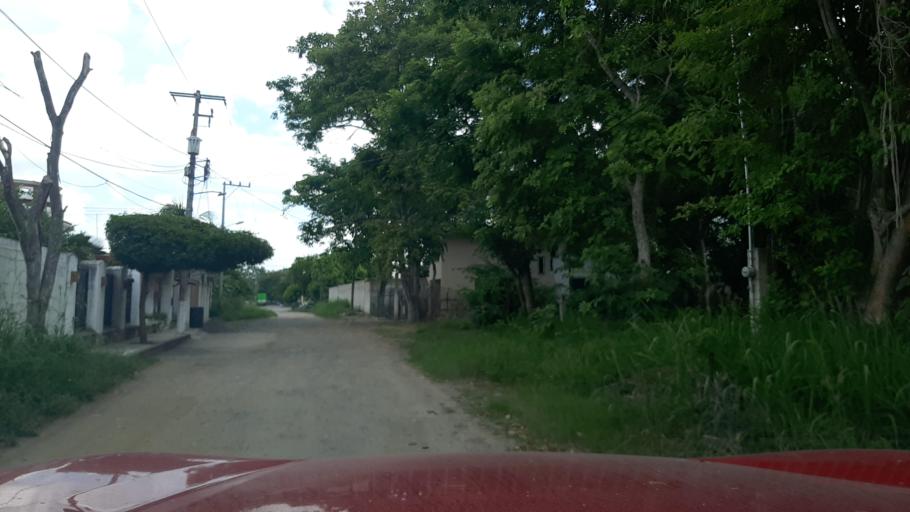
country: MX
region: Veracruz
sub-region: Poza Rica de Hidalgo
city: Villa de las Flores
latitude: 20.5713
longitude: -97.4335
